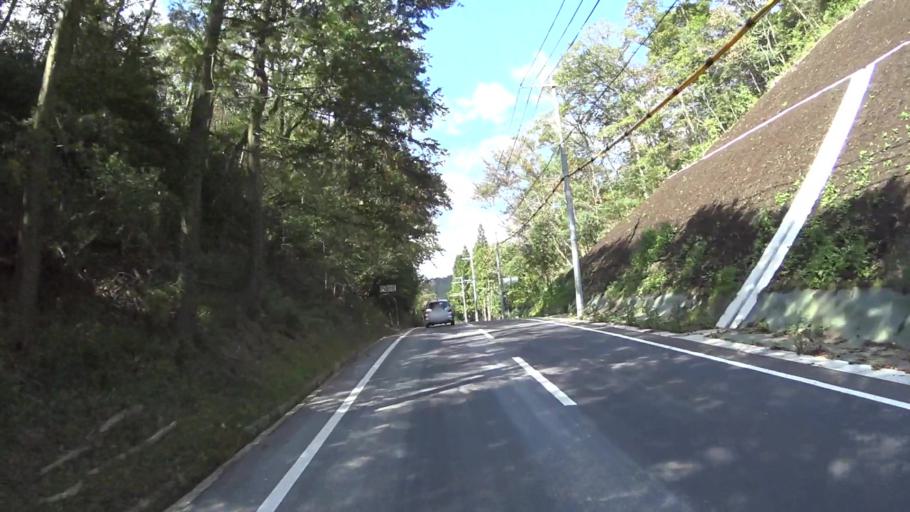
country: JP
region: Kyoto
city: Kameoka
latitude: 35.1639
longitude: 135.4589
